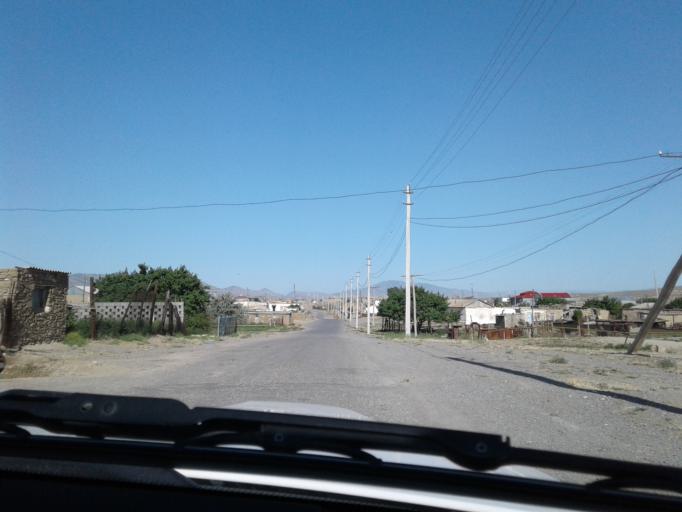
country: TM
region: Balkan
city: Magtymguly
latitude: 38.6833
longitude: 56.4557
